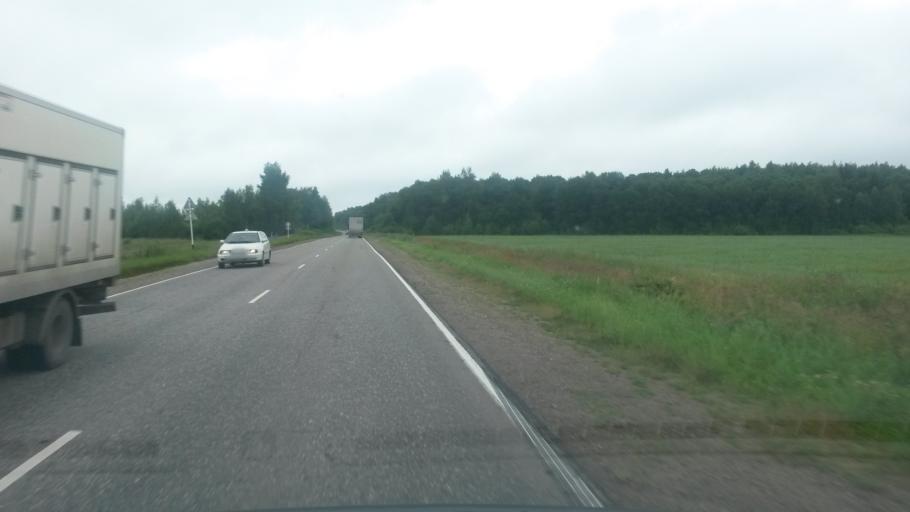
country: RU
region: Ivanovo
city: Pistsovo
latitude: 57.1276
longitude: 40.6046
